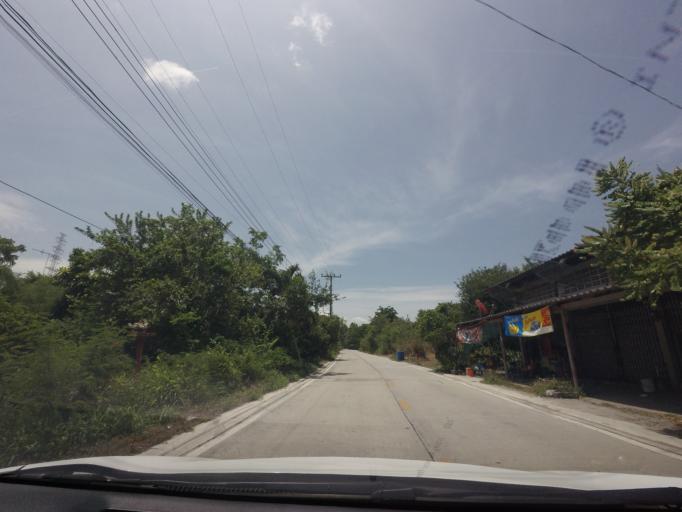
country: TH
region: Chon Buri
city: Chon Buri
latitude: 13.3240
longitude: 100.9757
